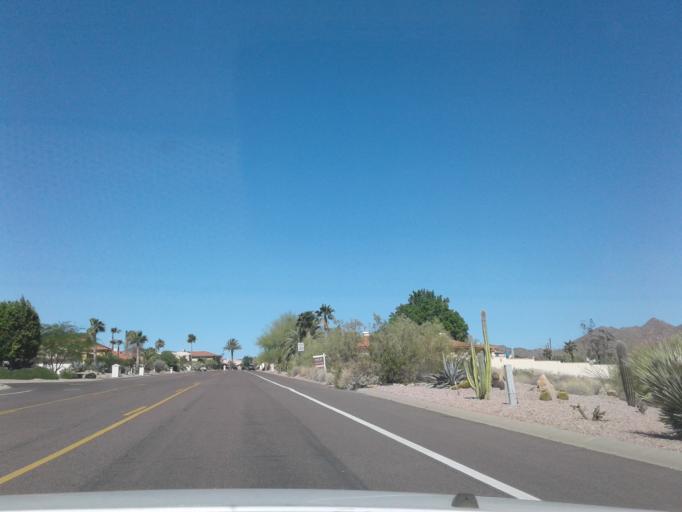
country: US
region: Arizona
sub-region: Maricopa County
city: Fountain Hills
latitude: 33.5915
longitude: -111.7452
